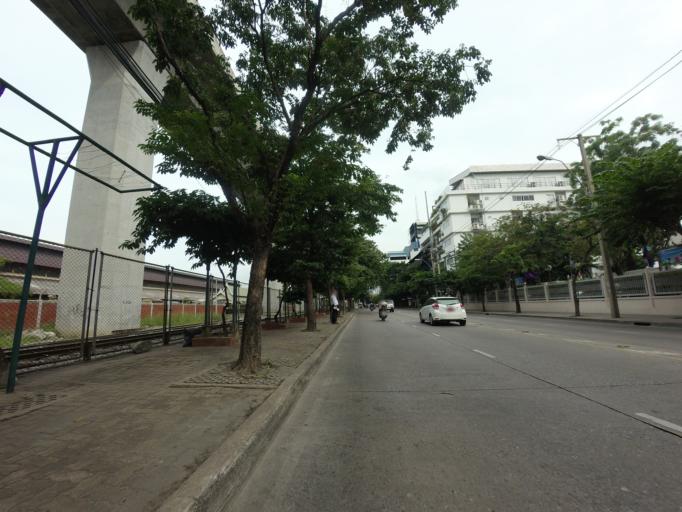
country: TH
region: Bangkok
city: Ratchathewi
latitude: 13.7546
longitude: 100.5438
